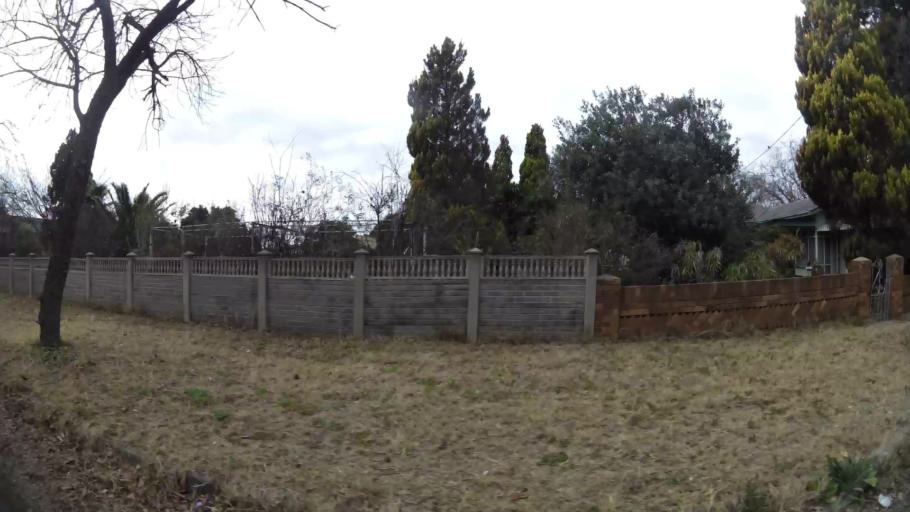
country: ZA
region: Orange Free State
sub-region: Fezile Dabi District Municipality
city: Kroonstad
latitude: -27.6345
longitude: 27.2322
